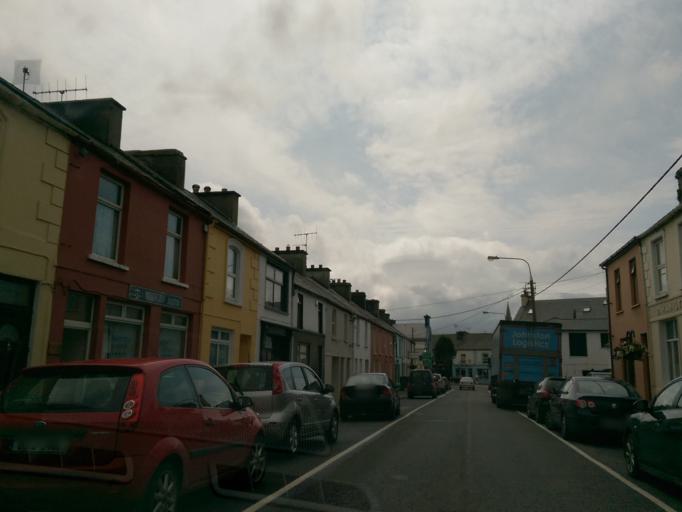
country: IE
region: Munster
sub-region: An Clar
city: Kilrush
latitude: 52.6402
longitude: -9.4839
